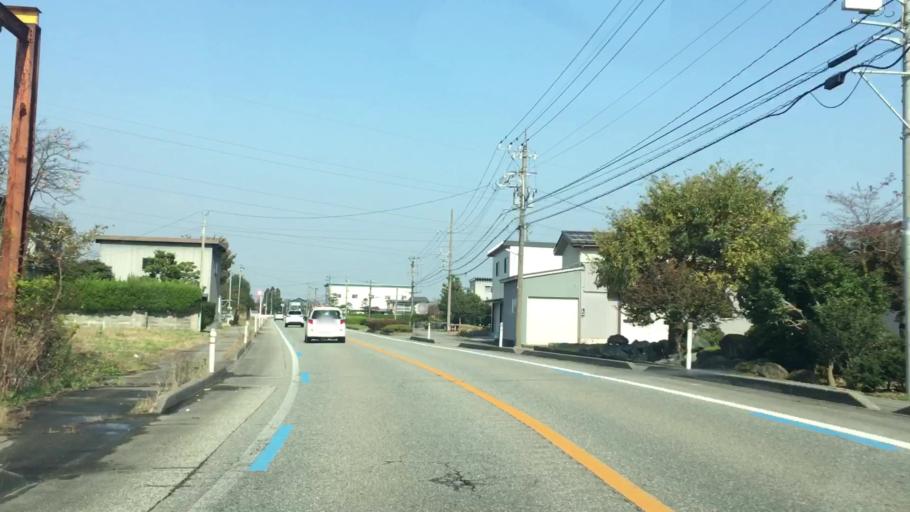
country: JP
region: Toyama
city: Toyama-shi
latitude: 36.6186
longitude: 137.1930
